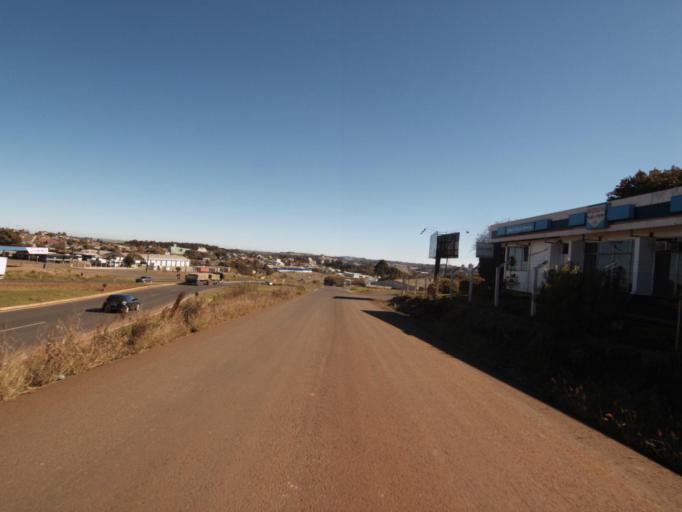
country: BR
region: Santa Catarina
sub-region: Xanxere
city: Xanxere
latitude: -26.8845
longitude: -52.3922
